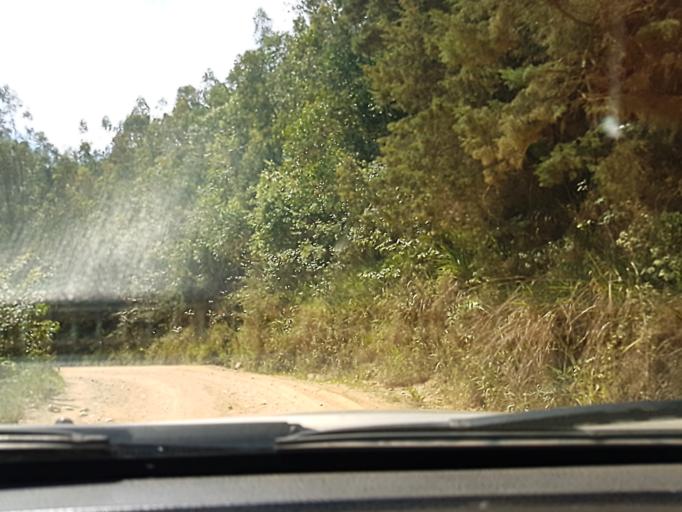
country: RW
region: Western Province
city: Cyangugu
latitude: -2.6995
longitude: 28.9084
